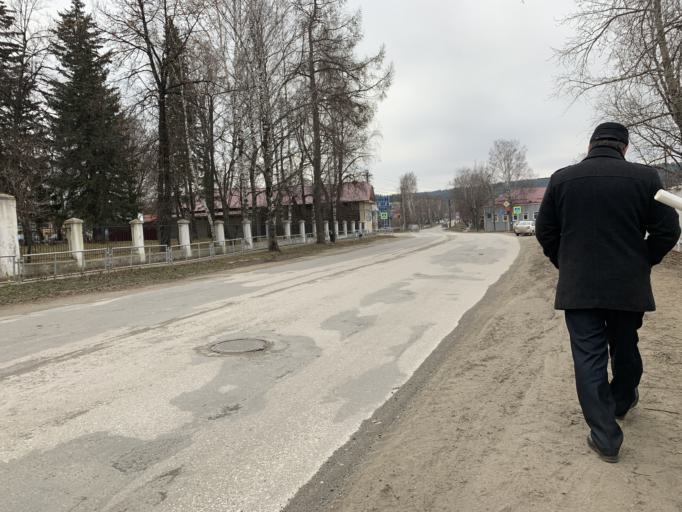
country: RU
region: Chelyabinsk
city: Nyazepetrovsk
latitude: 56.0536
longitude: 59.5927
